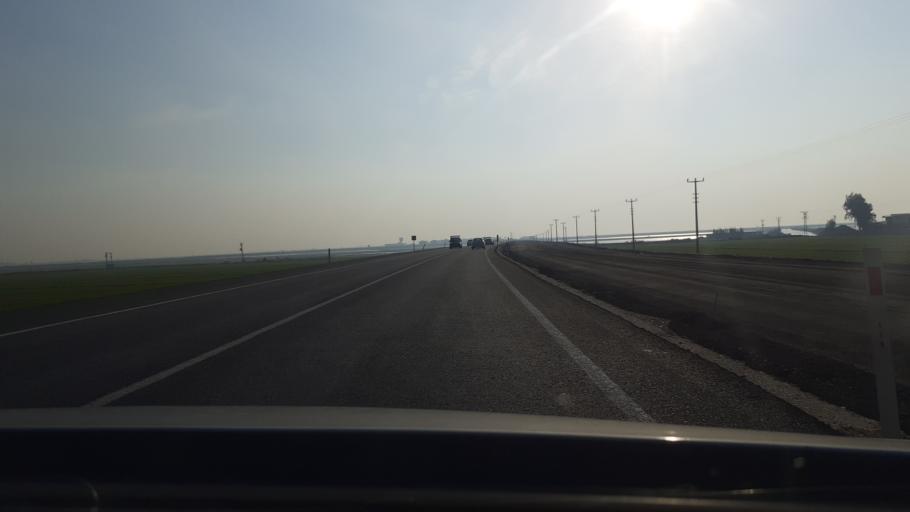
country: TR
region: Hatay
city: Serinyol
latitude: 36.3704
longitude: 36.2534
